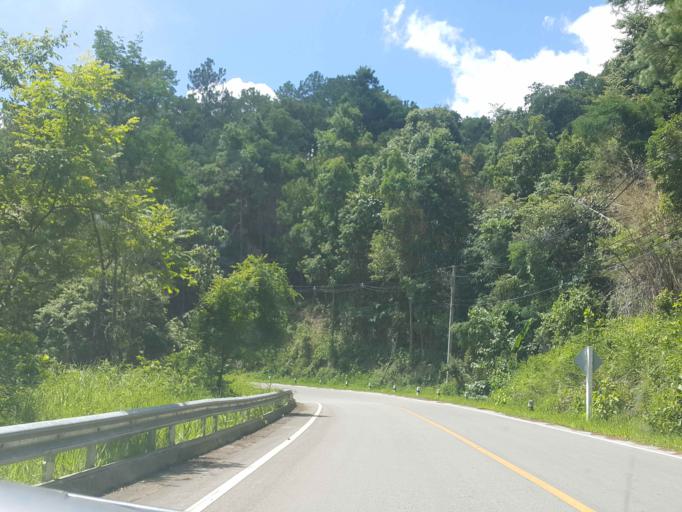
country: TH
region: Chiang Mai
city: Samoeng
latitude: 18.8741
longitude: 98.7814
